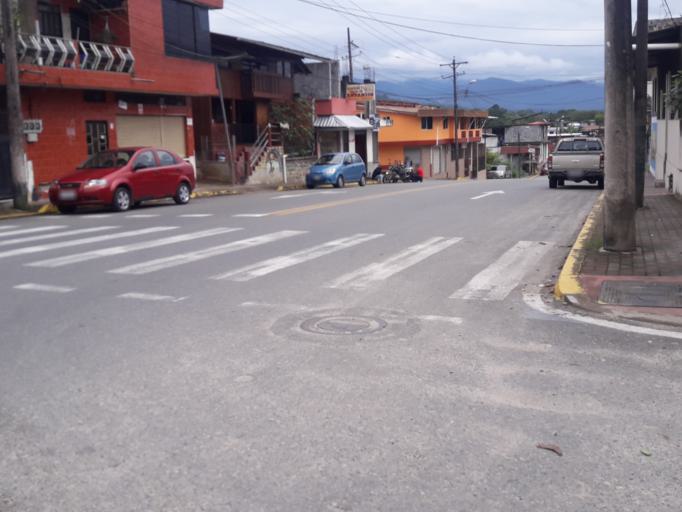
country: EC
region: Napo
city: Tena
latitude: -1.0024
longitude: -77.8141
